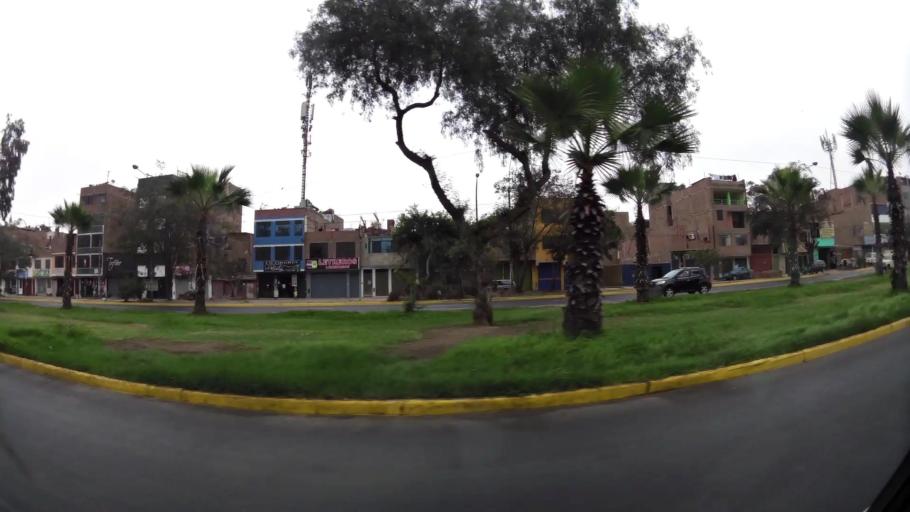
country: PE
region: Lima
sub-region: Lima
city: Independencia
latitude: -11.9674
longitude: -77.0746
